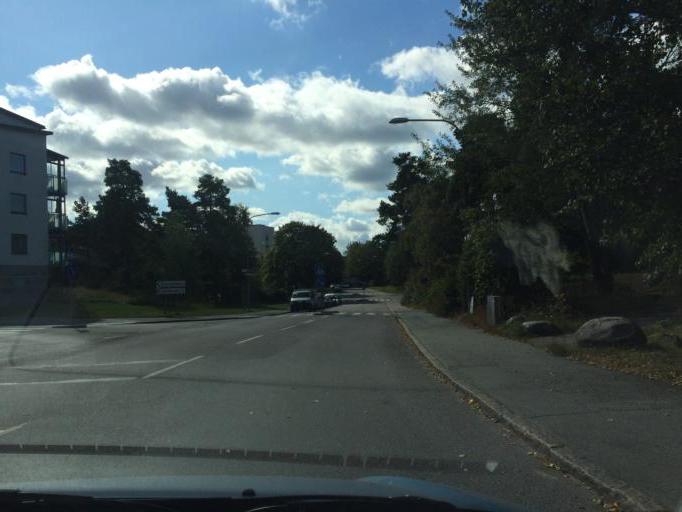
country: SE
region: Stockholm
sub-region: Nacka Kommun
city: Nacka
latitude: 59.2787
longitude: 18.1383
